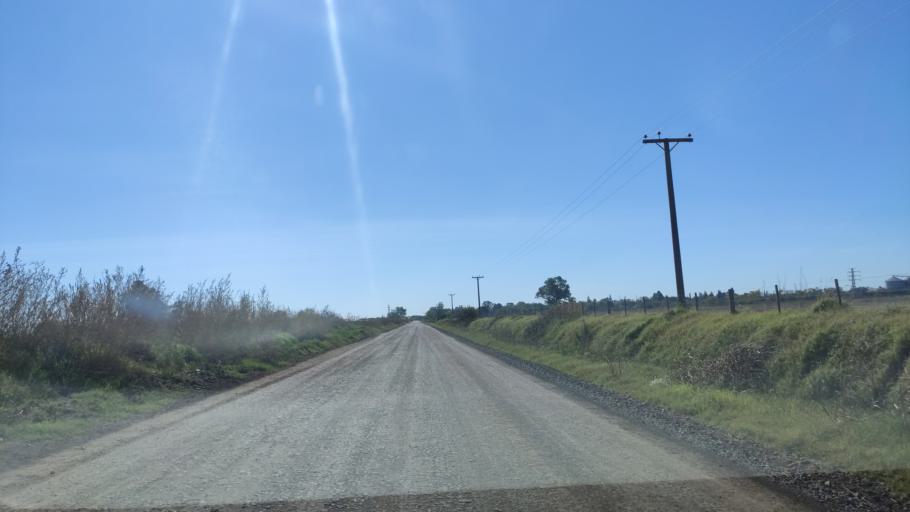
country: AR
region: Cordoba
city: Leones
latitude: -32.6695
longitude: -62.3125
